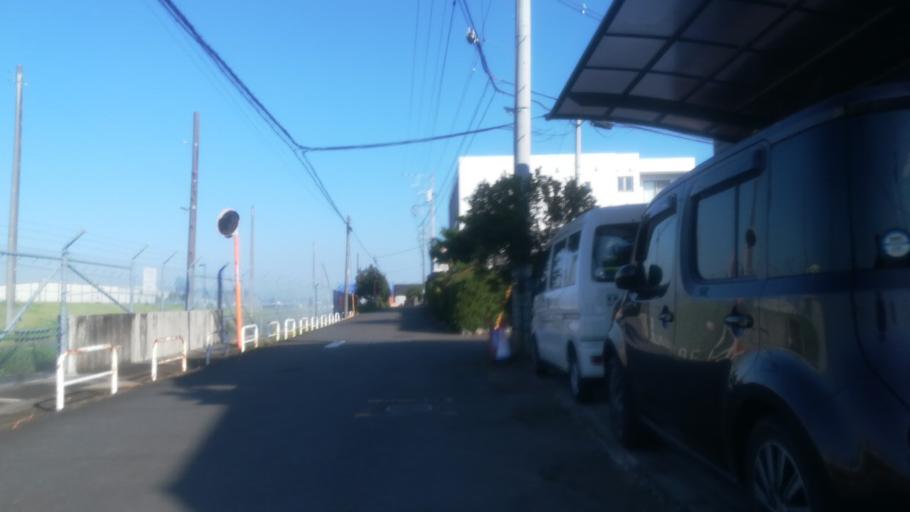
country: JP
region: Tokyo
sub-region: Machida-shi
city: Machida
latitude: 35.5823
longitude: 139.3901
